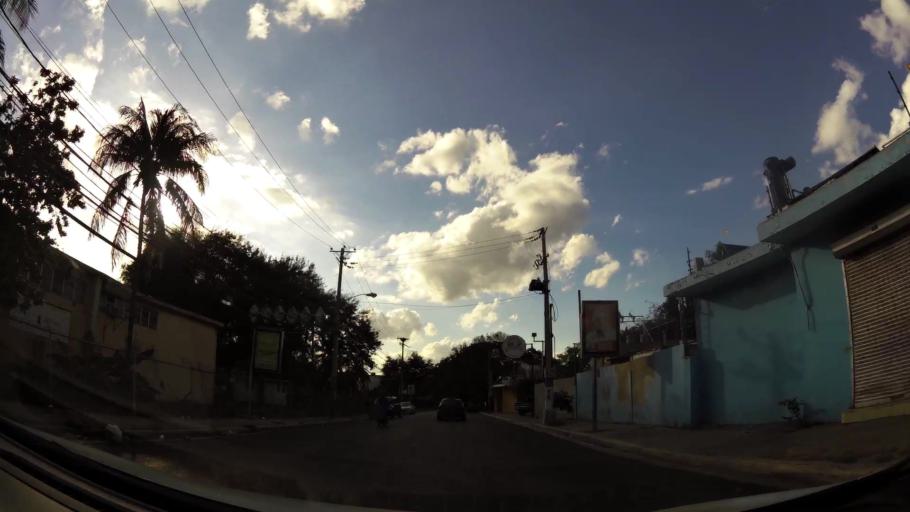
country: DO
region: Santiago
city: Santiago de los Caballeros
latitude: 19.4601
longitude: -70.7015
